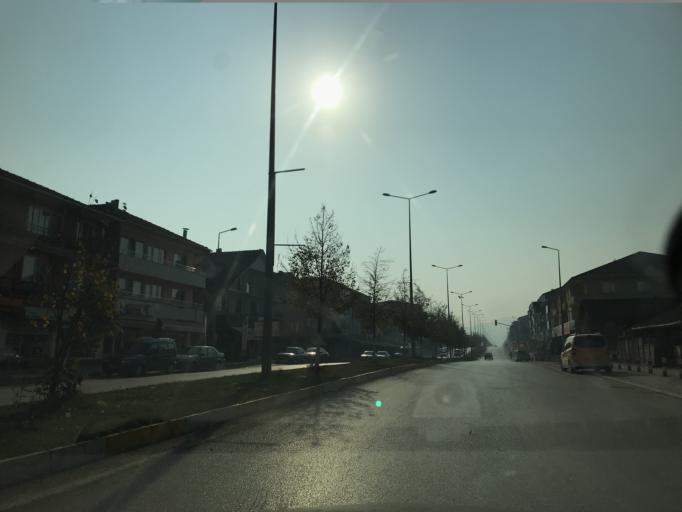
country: TR
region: Duzce
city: Cumayeri
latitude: 40.8729
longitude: 30.9508
